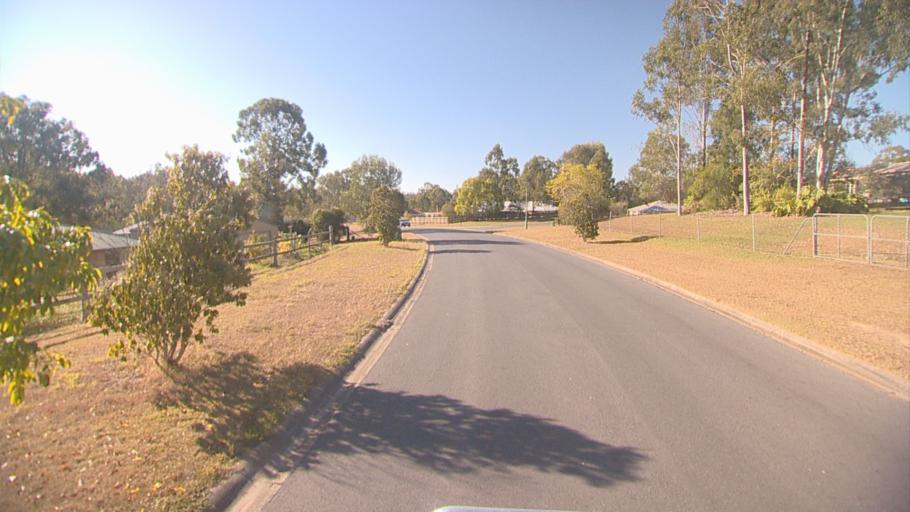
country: AU
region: Queensland
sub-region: Logan
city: Cedar Vale
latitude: -27.8634
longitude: 153.0379
